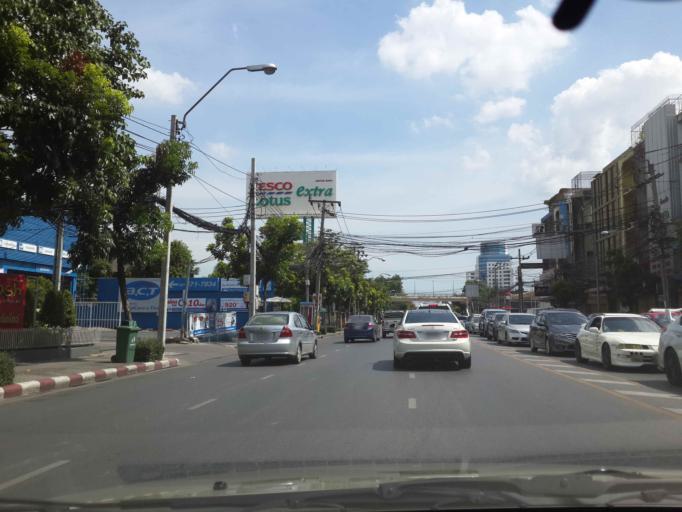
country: TH
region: Bangkok
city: Khlong Toei
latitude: 13.7187
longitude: 100.5671
